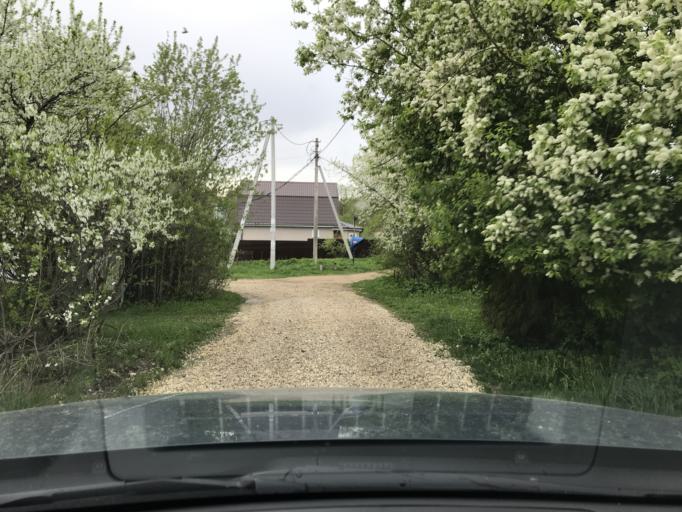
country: RU
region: Kaluga
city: Borovsk
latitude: 55.3203
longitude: 36.3496
